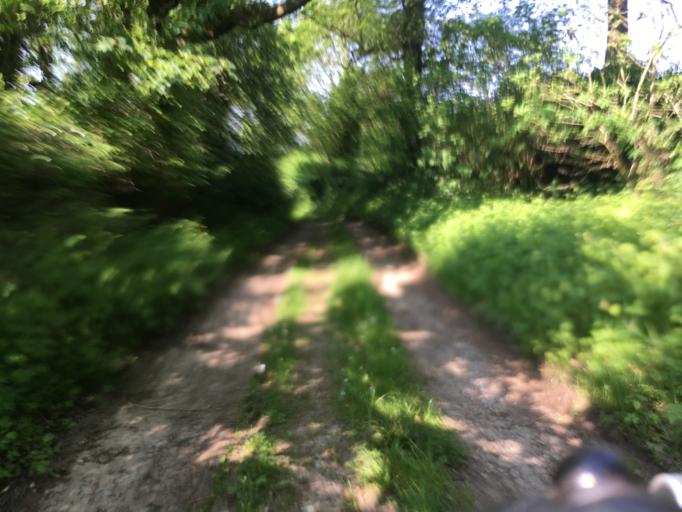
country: GB
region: England
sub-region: South Gloucestershire
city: Falfield
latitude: 51.6220
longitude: -2.4521
